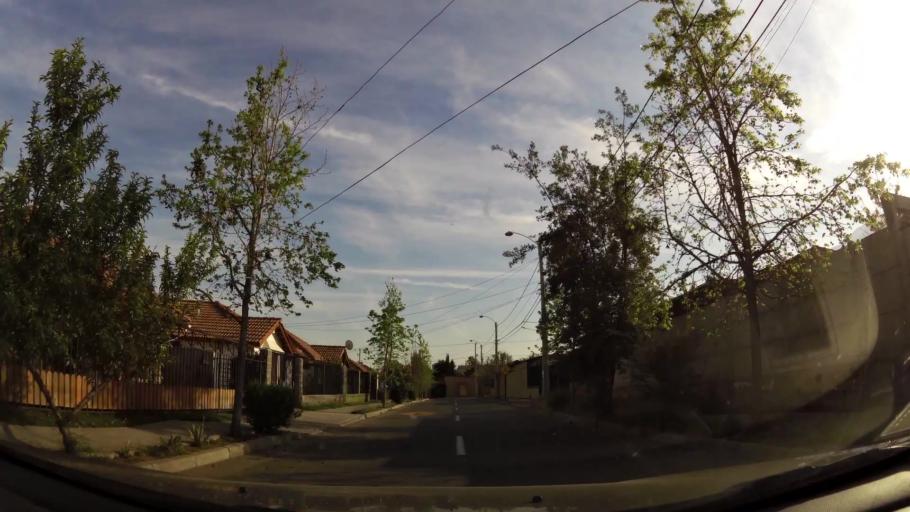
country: CL
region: Santiago Metropolitan
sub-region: Provincia de Cordillera
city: Puente Alto
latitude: -33.5689
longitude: -70.5457
